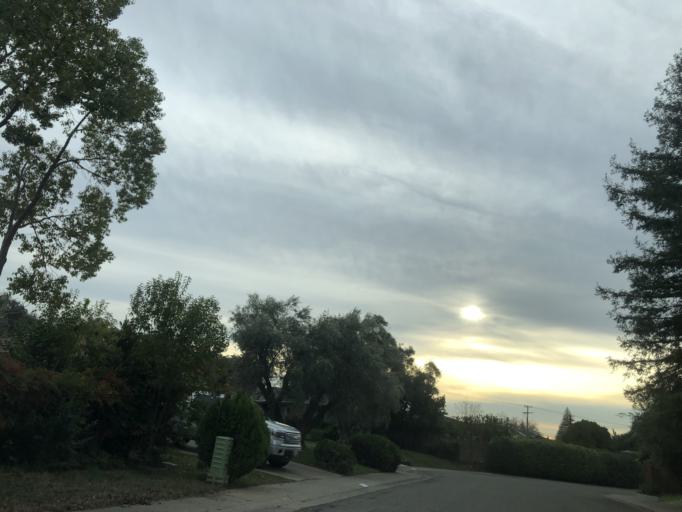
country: US
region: California
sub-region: Sacramento County
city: Foothill Farms
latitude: 38.6594
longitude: -121.3149
